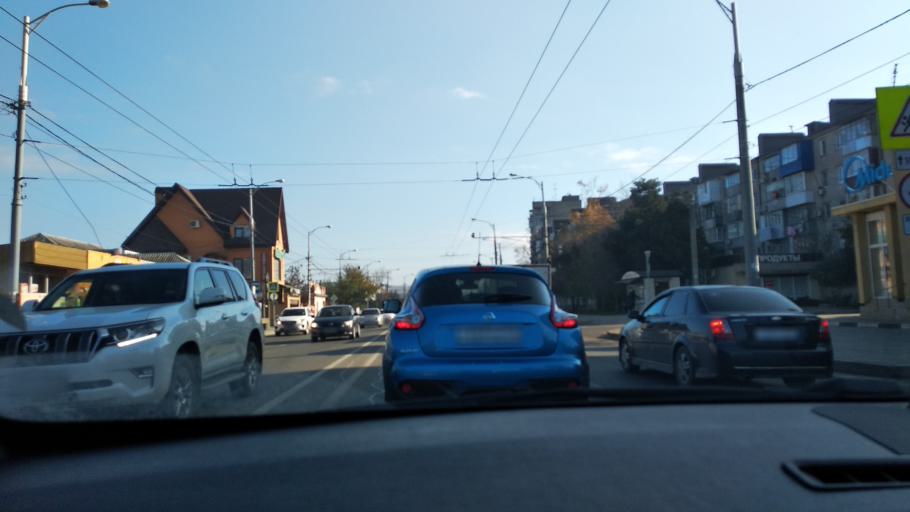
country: RU
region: Krasnodarskiy
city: Krasnodar
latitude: 45.0266
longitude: 39.0307
